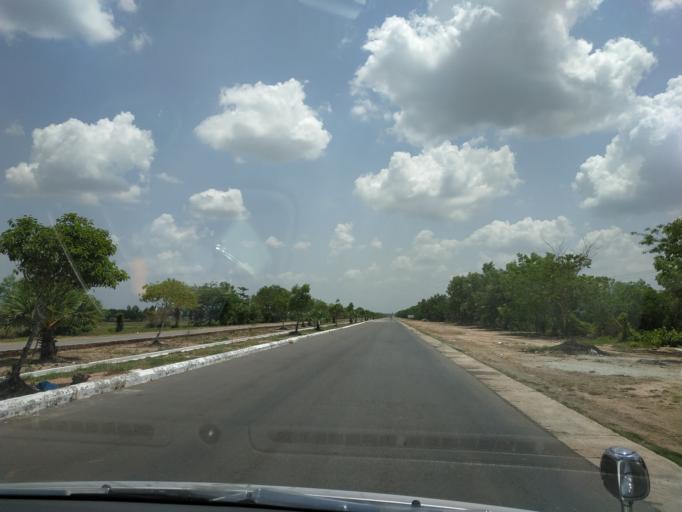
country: MM
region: Bago
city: Thanatpin
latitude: 17.0841
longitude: 96.1752
